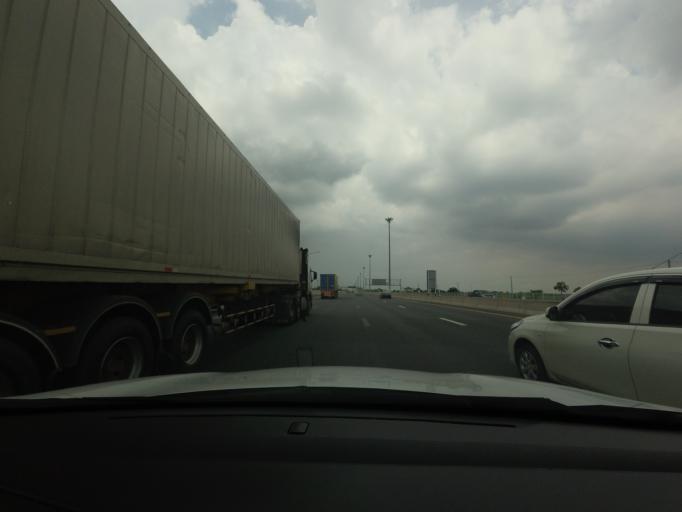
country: TH
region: Phra Nakhon Si Ayutthaya
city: Wang Noi
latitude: 14.1715
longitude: 100.6469
